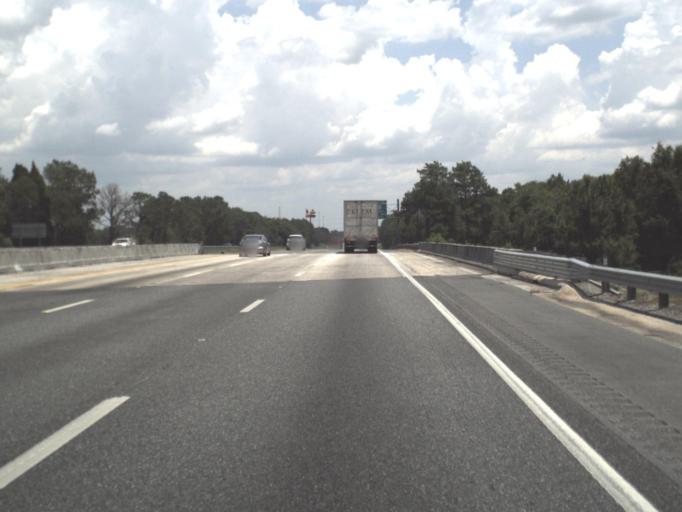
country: US
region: Florida
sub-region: Hamilton County
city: Jasper
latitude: 30.4572
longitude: -82.9472
